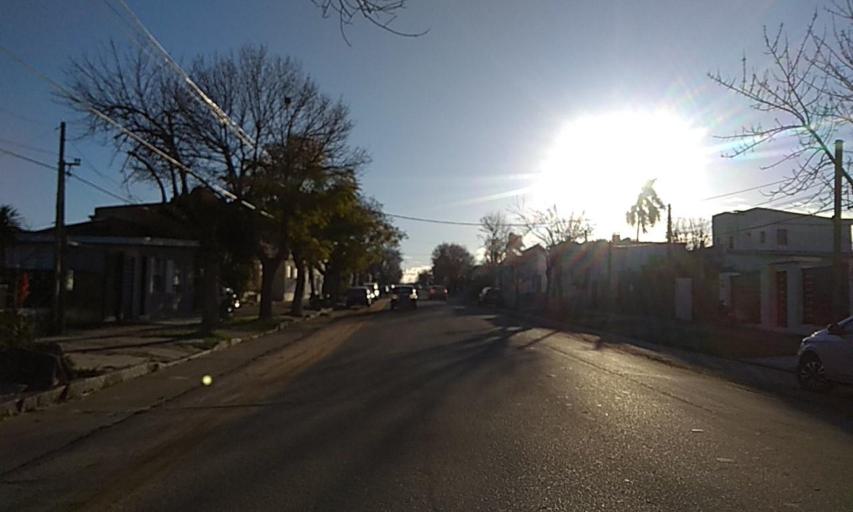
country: UY
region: Florida
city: Florida
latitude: -34.0994
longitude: -56.2246
